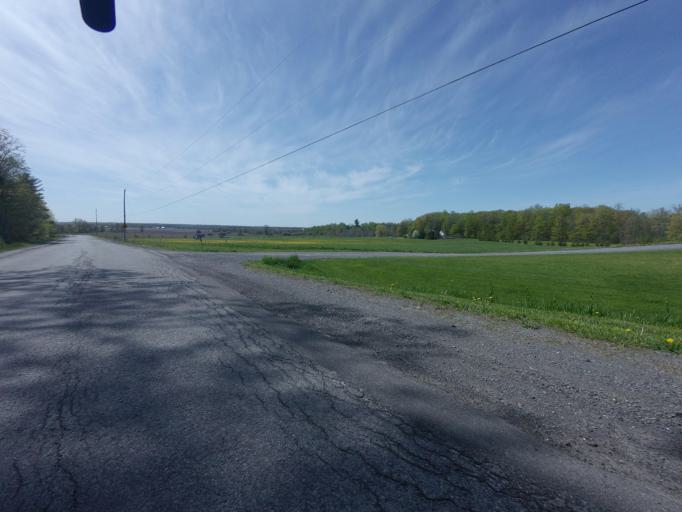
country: CA
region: Ontario
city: Arnprior
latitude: 45.4026
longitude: -76.2049
